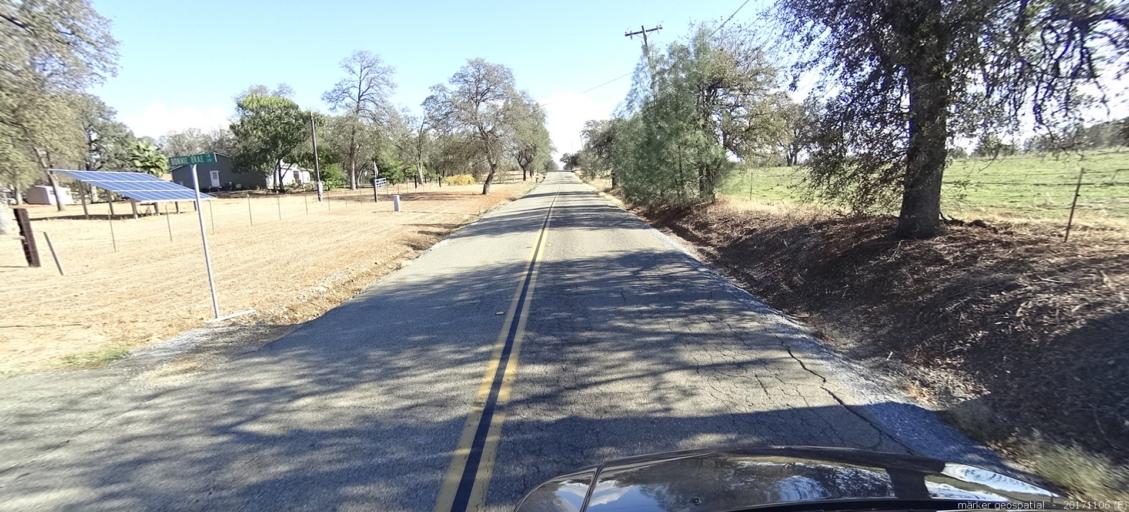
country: US
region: California
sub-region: Shasta County
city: Bella Vista
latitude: 40.6219
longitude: -122.2673
